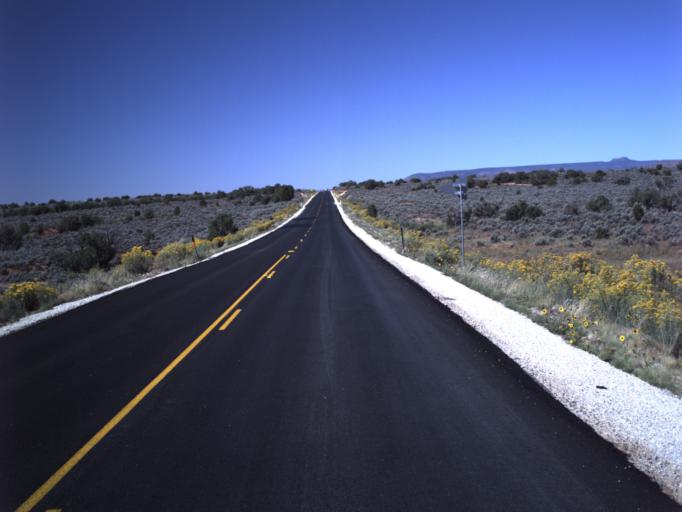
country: US
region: Utah
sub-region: San Juan County
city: Blanding
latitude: 37.5761
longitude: -109.5307
